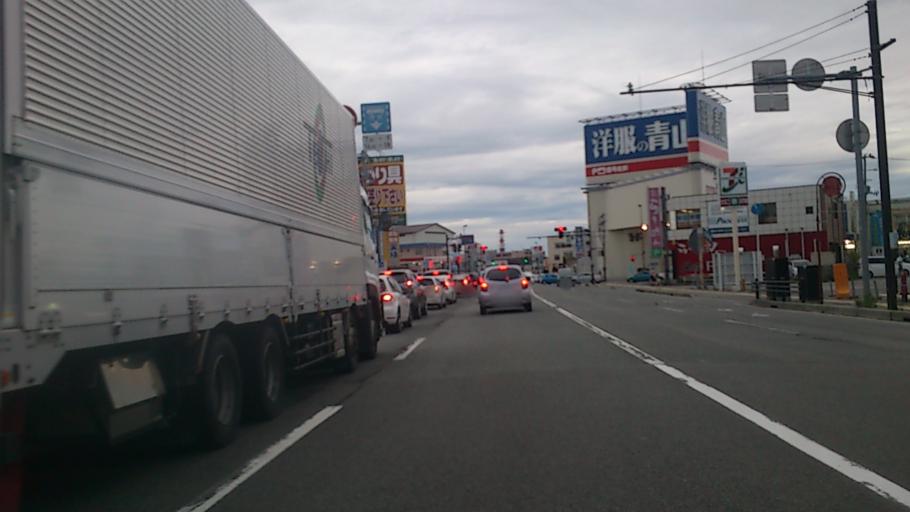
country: JP
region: Akita
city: Akita Shi
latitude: 39.7289
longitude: 140.1046
